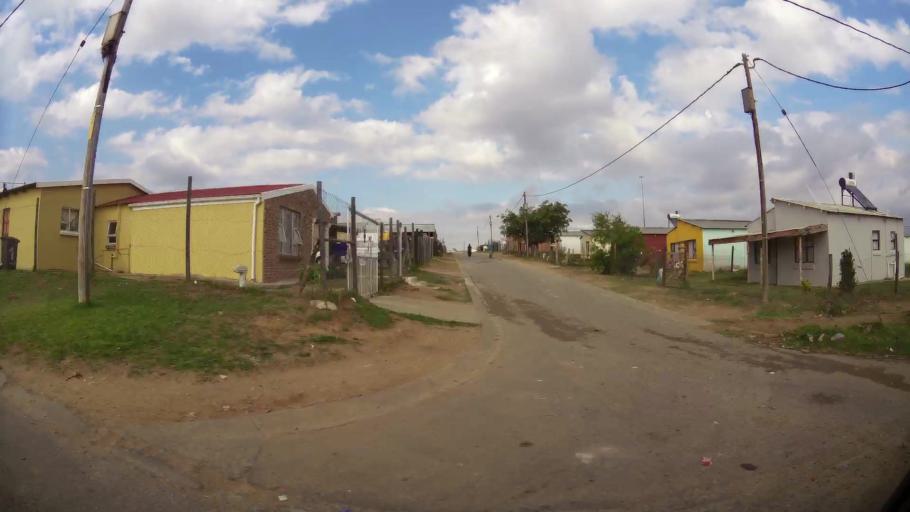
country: ZA
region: Eastern Cape
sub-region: Nelson Mandela Bay Metropolitan Municipality
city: Uitenhage
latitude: -33.7464
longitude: 25.3943
